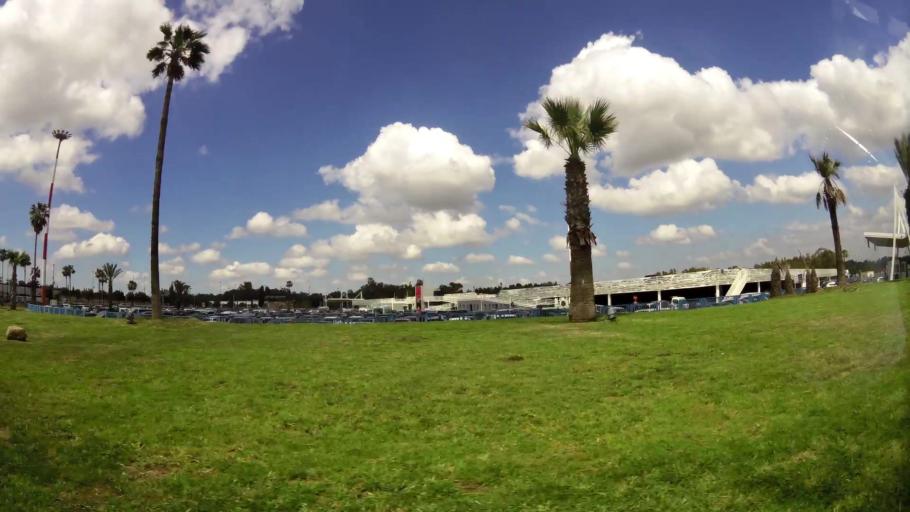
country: MA
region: Chaouia-Ouardigha
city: Nouaseur
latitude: 33.3746
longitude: -7.5801
